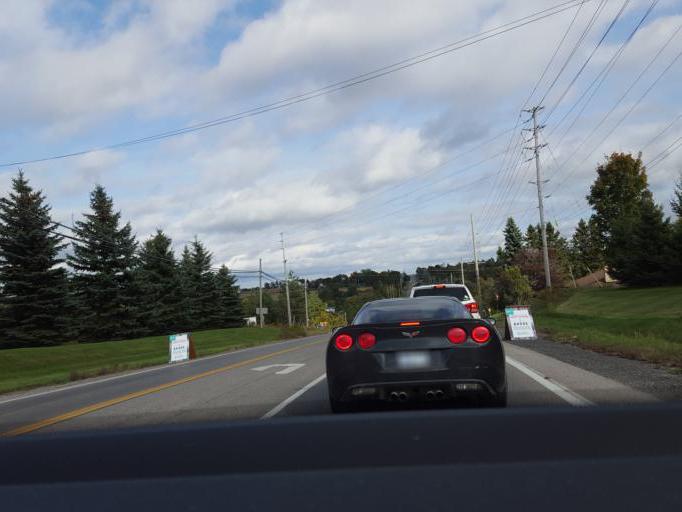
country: CA
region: Ontario
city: Oshawa
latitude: 43.9471
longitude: -78.8160
